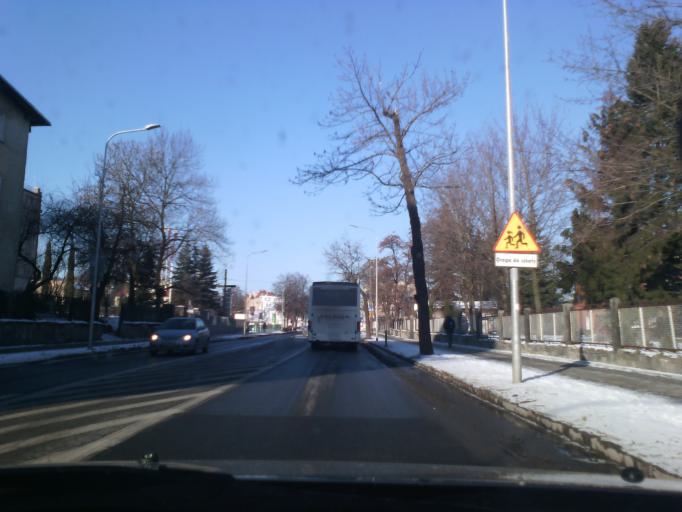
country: PL
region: Lower Silesian Voivodeship
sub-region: Powiat swidnicki
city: Strzegom
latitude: 50.9624
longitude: 16.3480
